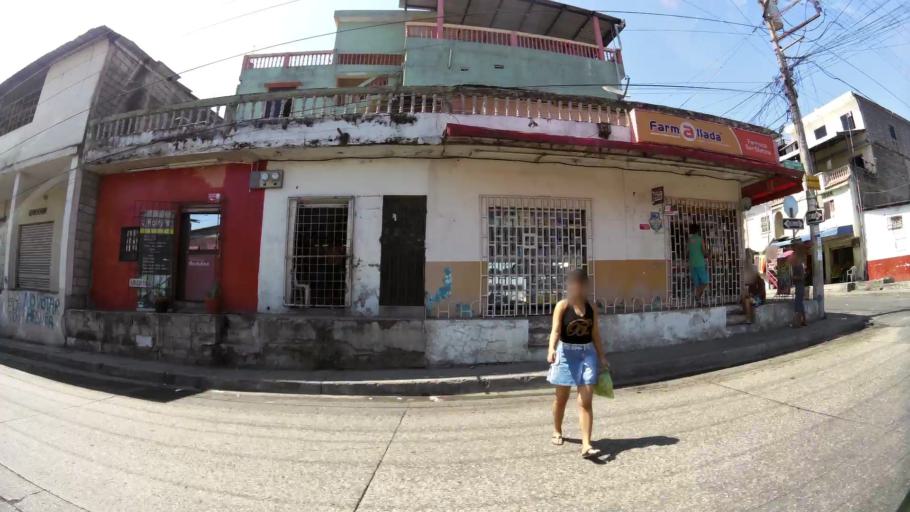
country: EC
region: Guayas
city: Guayaquil
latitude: -2.1293
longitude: -79.9194
